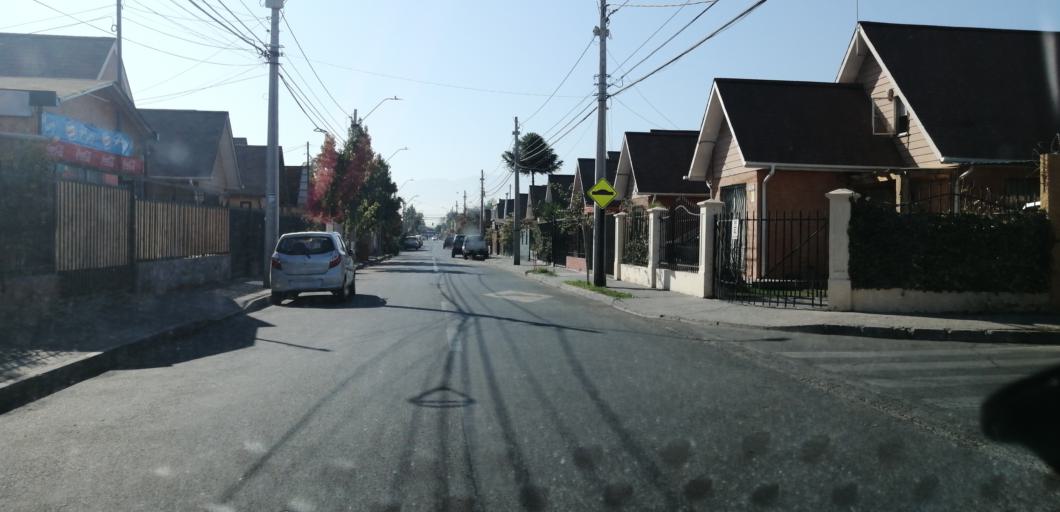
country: CL
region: Santiago Metropolitan
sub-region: Provincia de Santiago
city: Lo Prado
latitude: -33.4345
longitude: -70.7766
